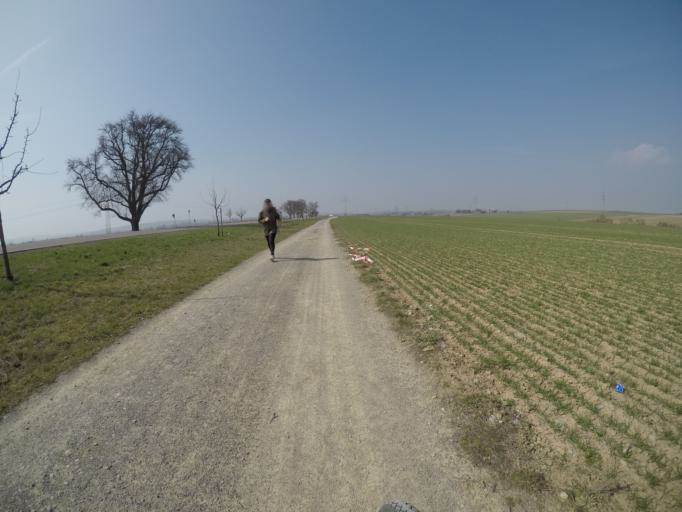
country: DE
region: Baden-Wuerttemberg
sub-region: Regierungsbezirk Stuttgart
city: Herrenberg
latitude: 48.6173
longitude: 8.8676
